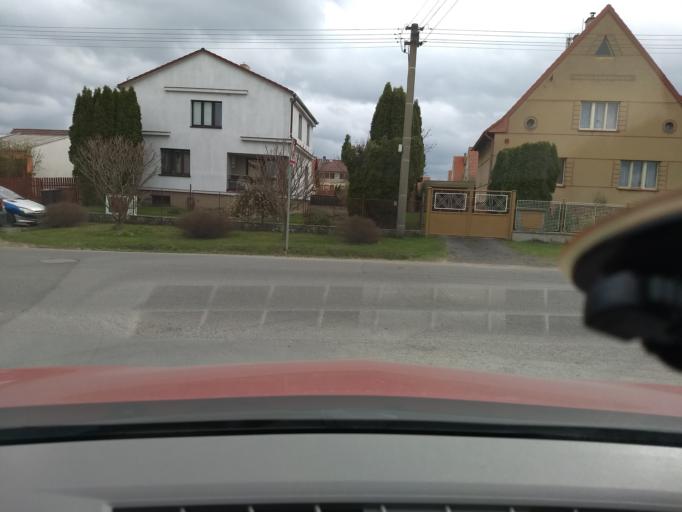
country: CZ
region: Central Bohemia
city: Unhost'
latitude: 50.0682
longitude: 14.1653
